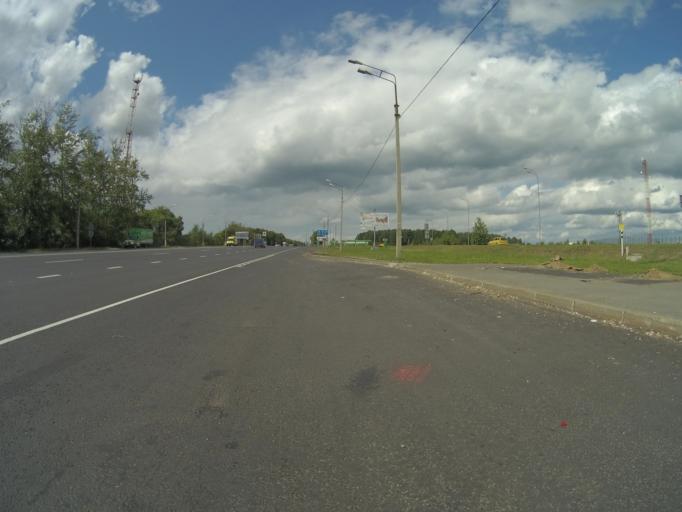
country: RU
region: Vladimir
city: Kommunar
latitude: 56.1759
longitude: 40.4566
